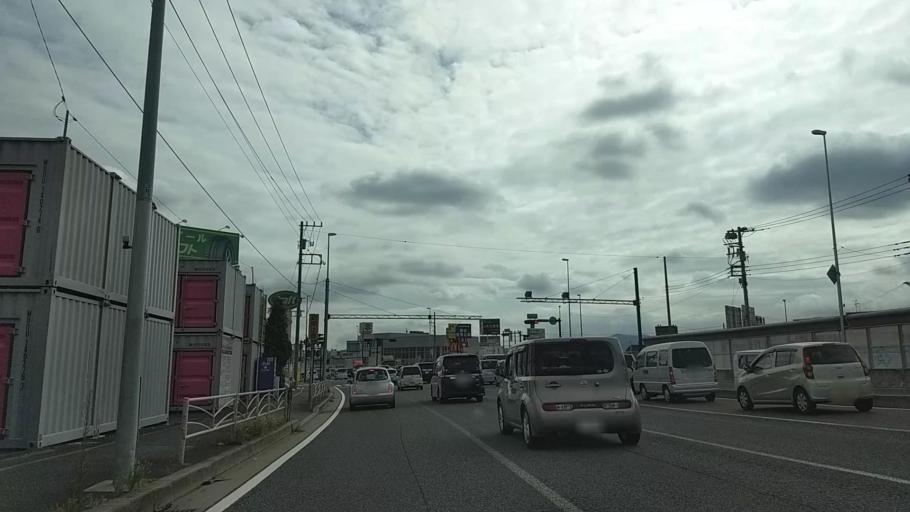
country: JP
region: Kanagawa
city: Atsugi
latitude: 35.4636
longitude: 139.3610
